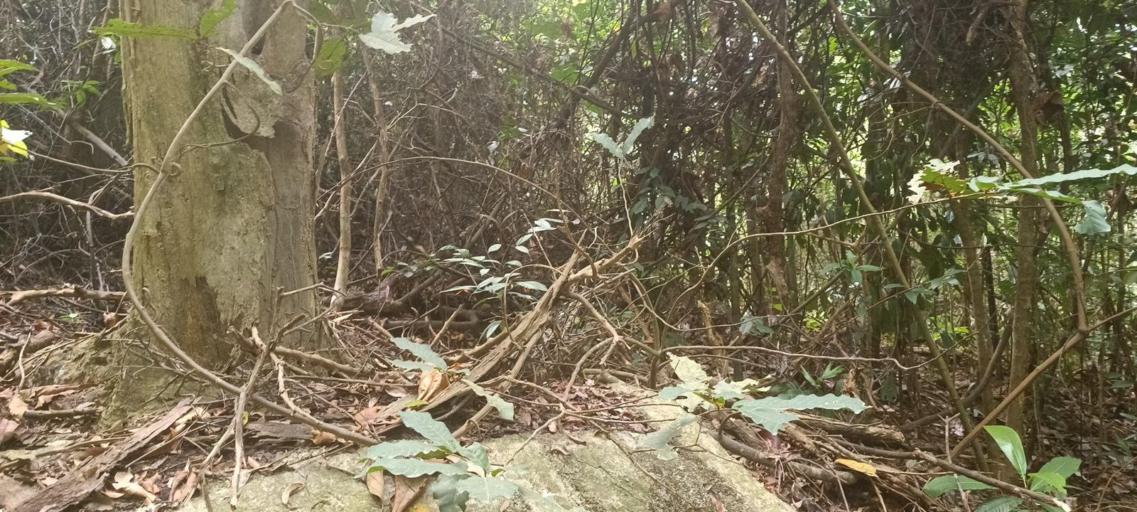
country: MY
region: Penang
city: Bukit Mertajam
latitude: 5.3732
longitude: 100.4987
